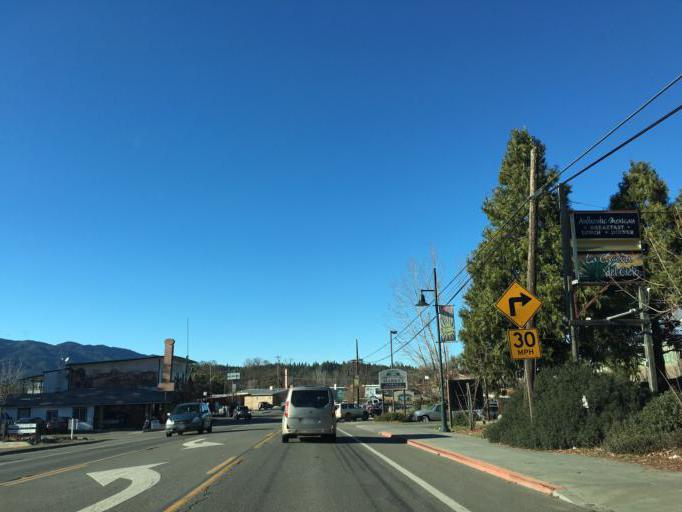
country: US
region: California
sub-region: Mendocino County
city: Laytonville
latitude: 39.6866
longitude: -123.4817
